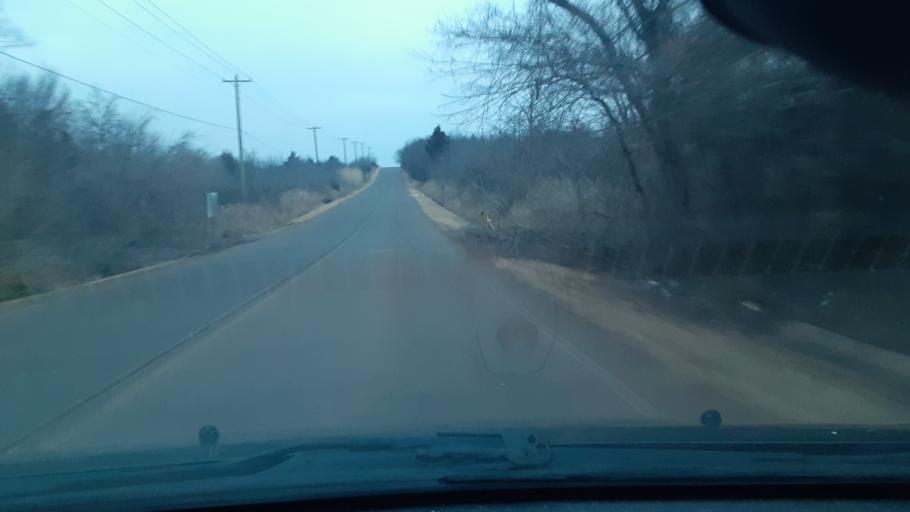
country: US
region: Oklahoma
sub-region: Logan County
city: Guthrie
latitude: 35.8593
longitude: -97.4076
